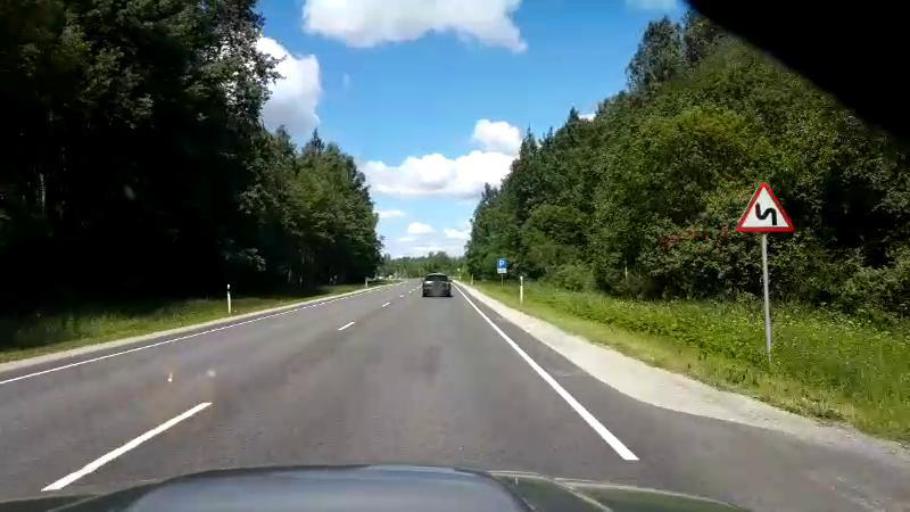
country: EE
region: Paernumaa
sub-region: Sauga vald
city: Sauga
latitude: 58.4433
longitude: 24.4987
